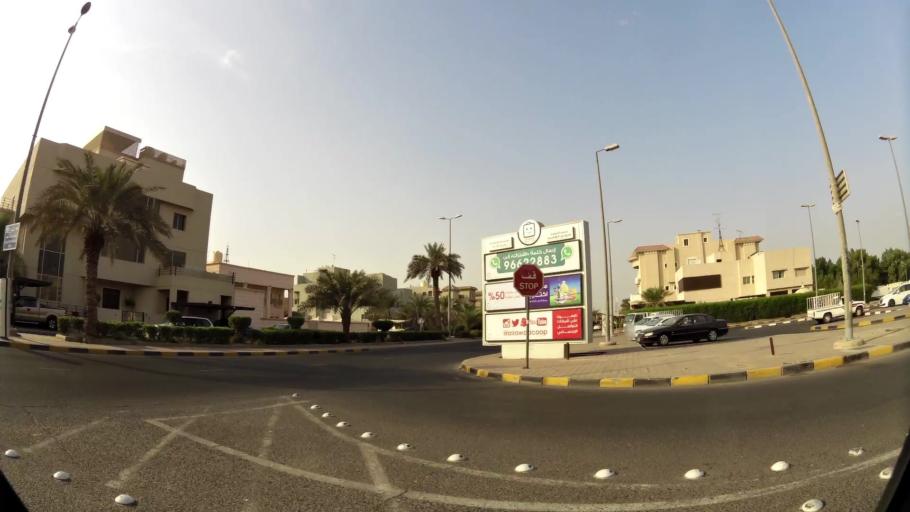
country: KW
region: Muhafazat Hawalli
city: Hawalli
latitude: 29.3233
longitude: 48.0029
